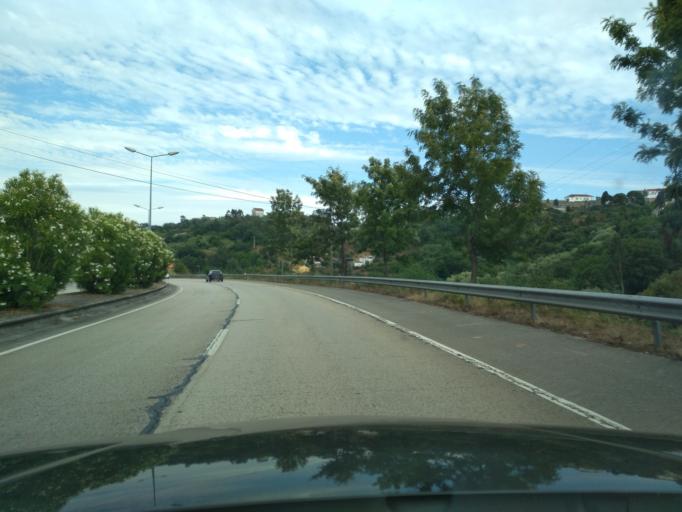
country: PT
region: Coimbra
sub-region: Coimbra
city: Coimbra
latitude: 40.2248
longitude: -8.4066
